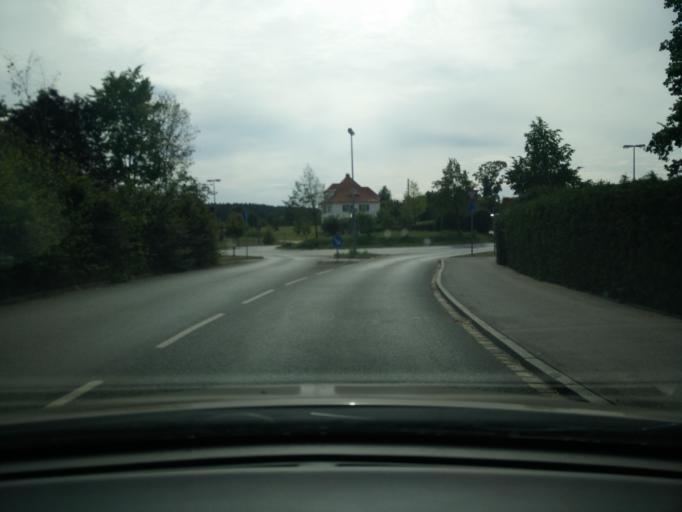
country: DE
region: Bavaria
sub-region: Regierungsbezirk Mittelfranken
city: Seukendorf
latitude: 49.4860
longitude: 10.8768
